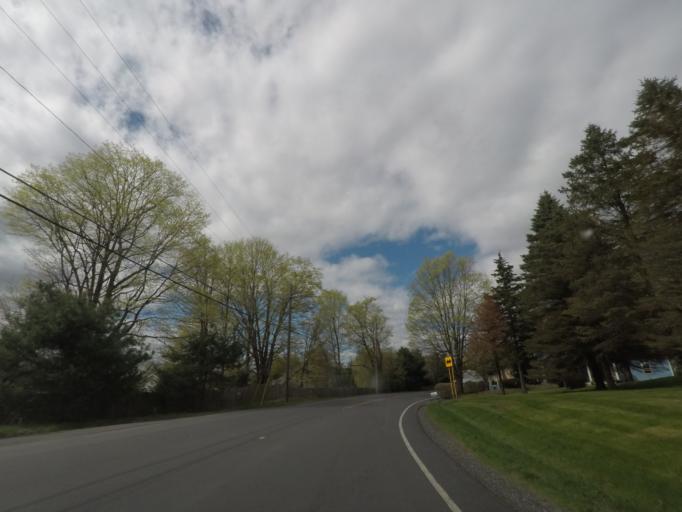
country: US
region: New York
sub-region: Columbia County
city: Valatie
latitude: 42.4061
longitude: -73.6752
